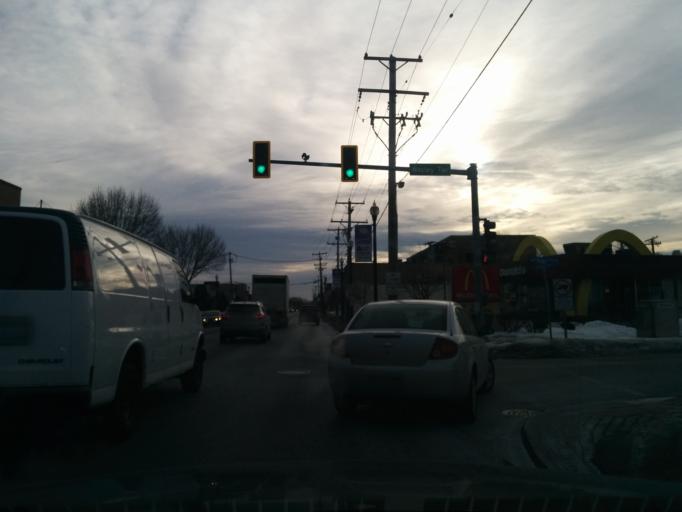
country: US
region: Illinois
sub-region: Cook County
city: Schiller Park
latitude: 41.9545
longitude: -87.8641
